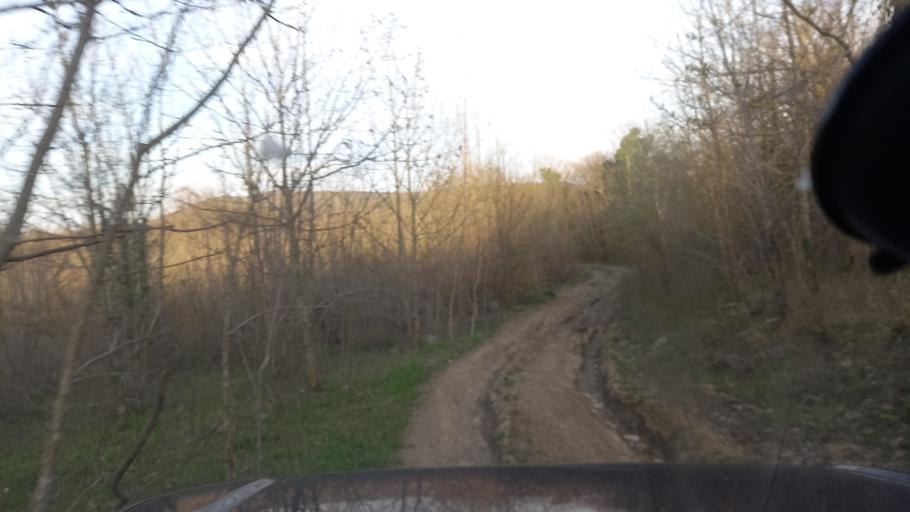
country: RU
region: Krasnodarskiy
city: Arkhipo-Osipovka
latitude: 44.3606
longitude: 38.5600
